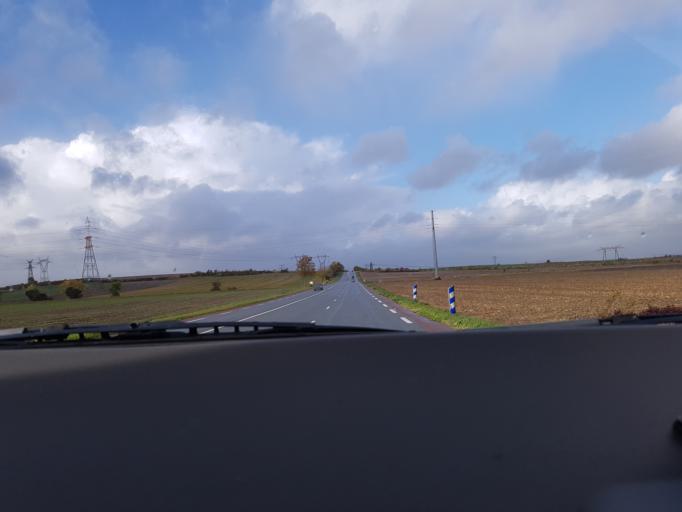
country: FR
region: Poitou-Charentes
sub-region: Departement de la Charente-Maritime
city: Les Gonds
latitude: 45.6669
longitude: -0.5975
